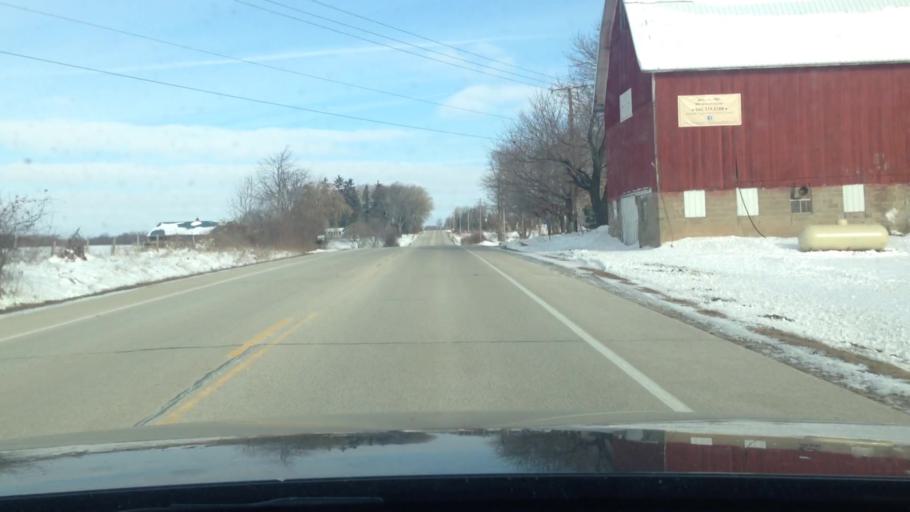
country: US
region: Wisconsin
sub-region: Walworth County
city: Lake Geneva
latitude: 42.6582
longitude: -88.4137
